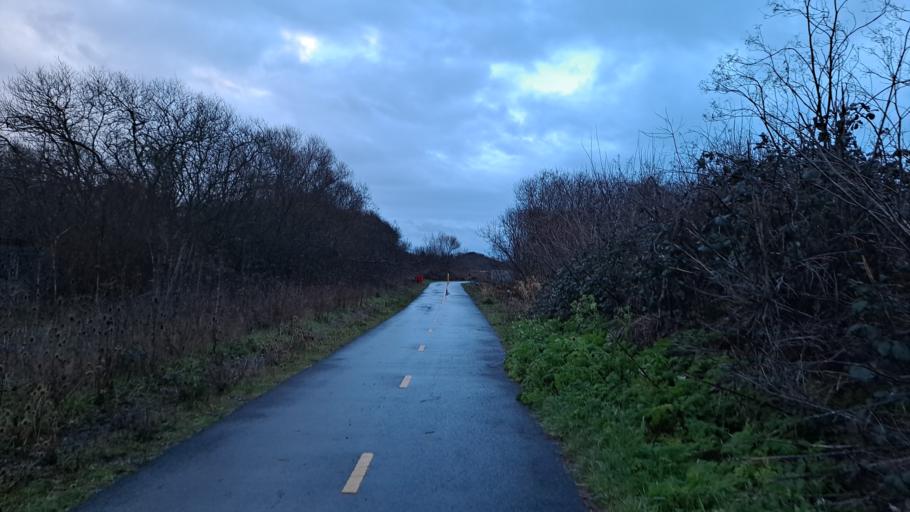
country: US
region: California
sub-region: Humboldt County
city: Arcata
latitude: 40.8642
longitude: -124.0931
